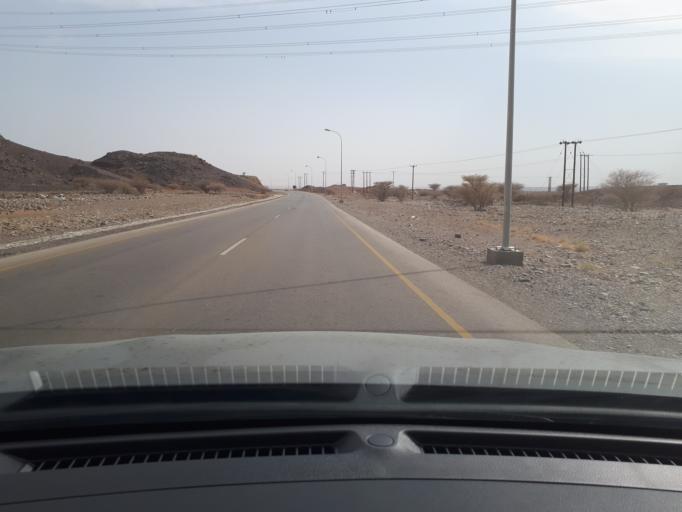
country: OM
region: Ash Sharqiyah
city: Badiyah
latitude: 22.5247
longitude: 58.9516
